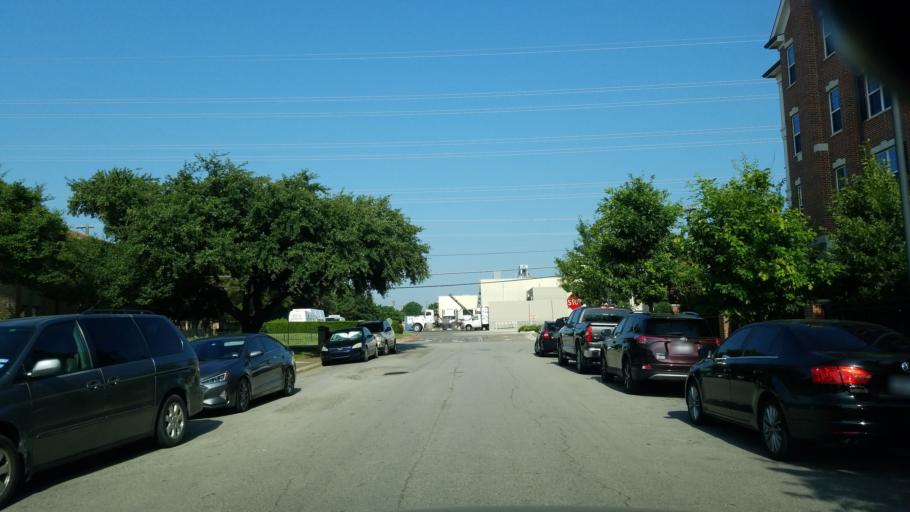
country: US
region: Texas
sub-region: Dallas County
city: Highland Park
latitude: 32.8492
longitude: -96.7671
